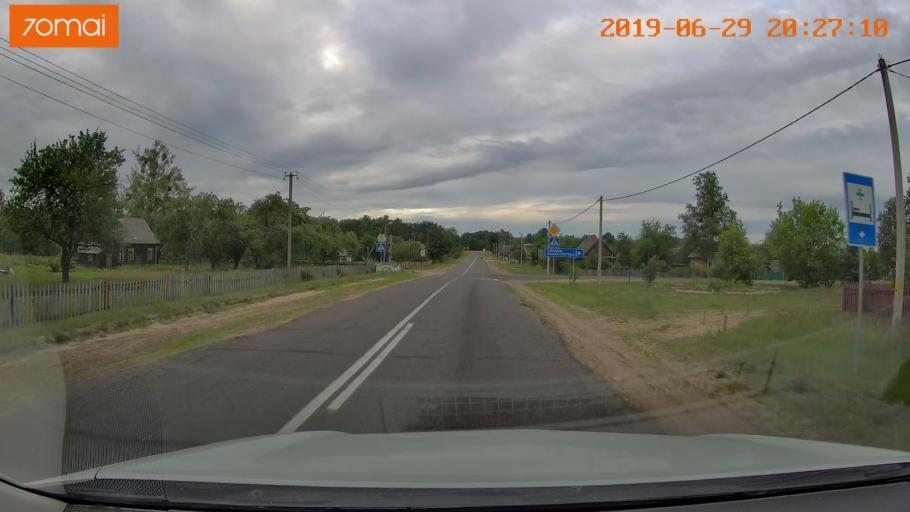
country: BY
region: Brest
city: Hantsavichy
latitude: 52.4720
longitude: 26.3022
